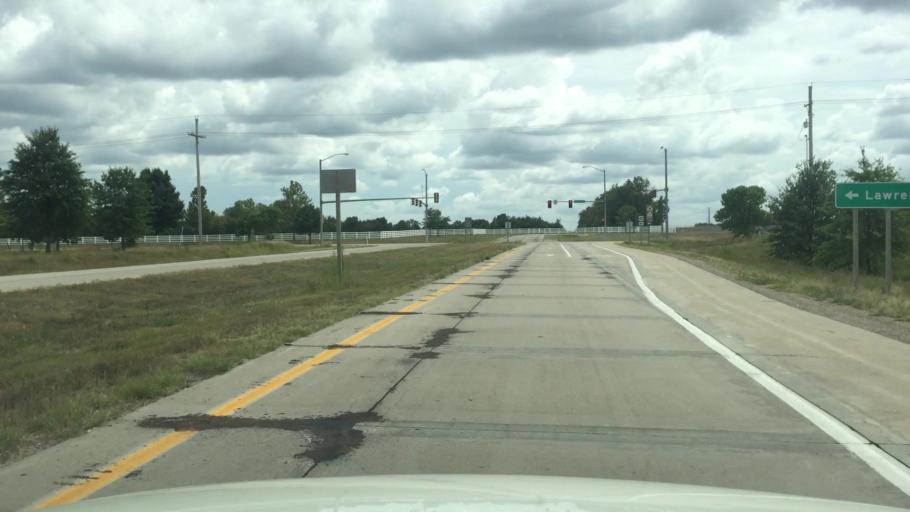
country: US
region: Kansas
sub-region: Shawnee County
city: Topeka
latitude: 39.0455
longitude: -95.5994
